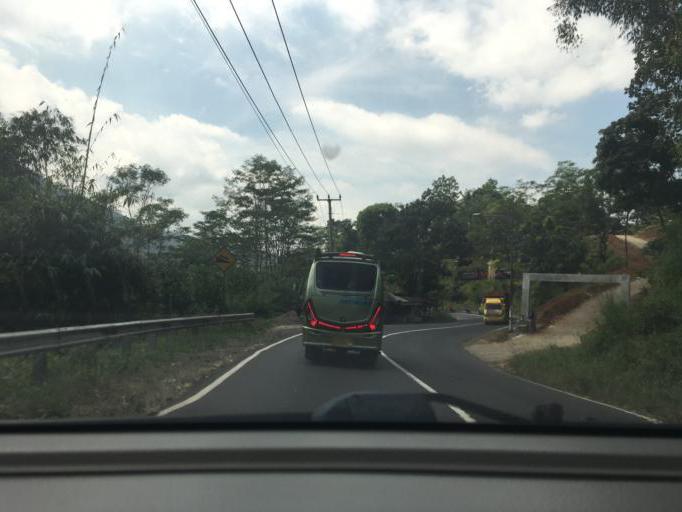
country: ID
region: West Java
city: Wage Cibahayu
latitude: -7.1163
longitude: 108.1211
